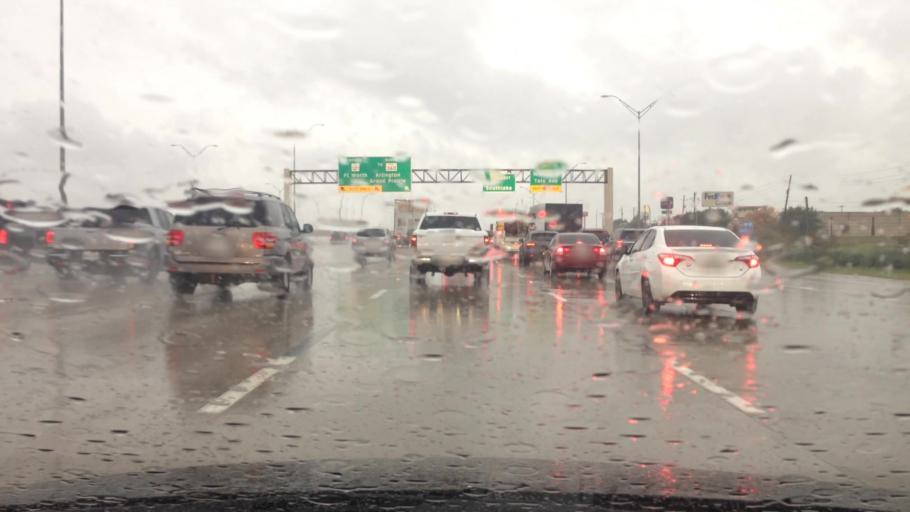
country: US
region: Texas
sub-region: Tarrant County
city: Grapevine
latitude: 32.9232
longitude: -97.0731
